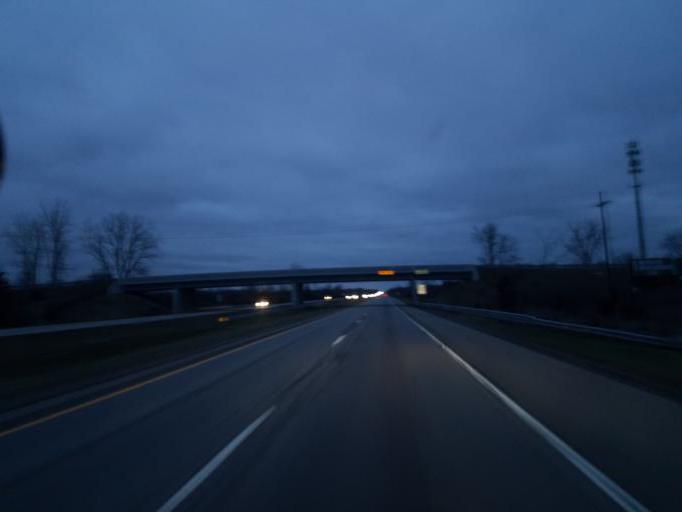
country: US
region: Michigan
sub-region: Washtenaw County
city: Milan
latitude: 42.1119
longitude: -83.6822
